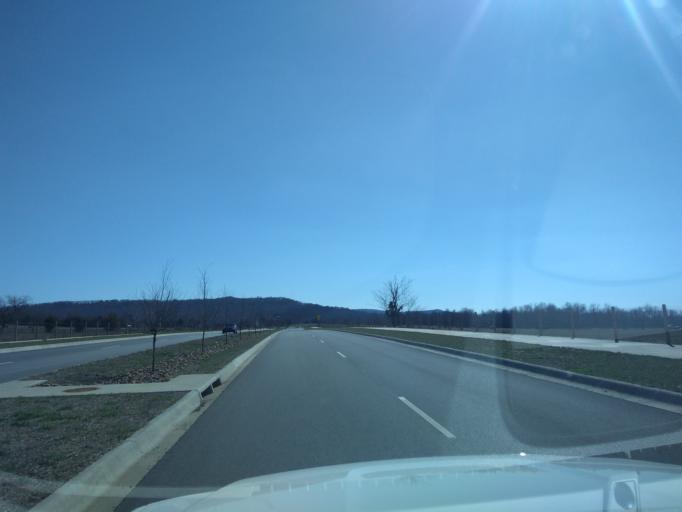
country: US
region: Arkansas
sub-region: Washington County
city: Farmington
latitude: 36.0607
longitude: -94.2204
